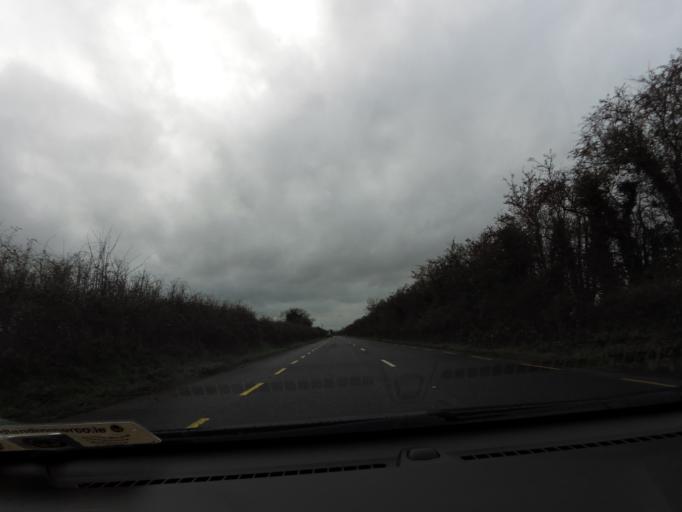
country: IE
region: Leinster
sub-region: Kilkenny
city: Ballyragget
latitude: 52.7706
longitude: -7.3318
